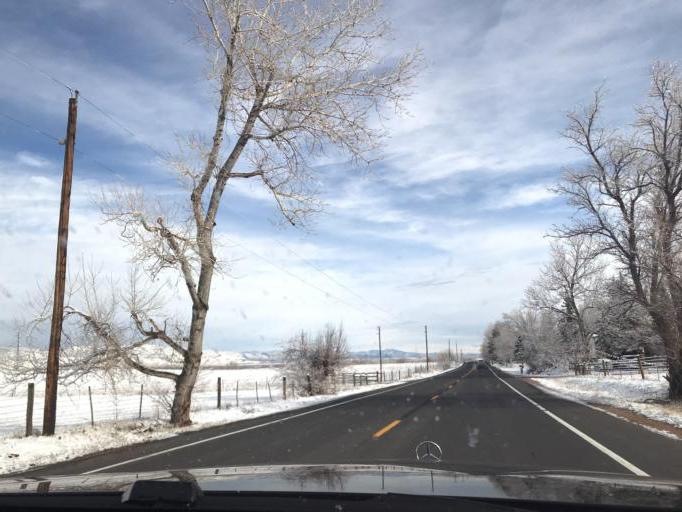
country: US
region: Colorado
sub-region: Boulder County
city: Superior
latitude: 39.9708
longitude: -105.2128
